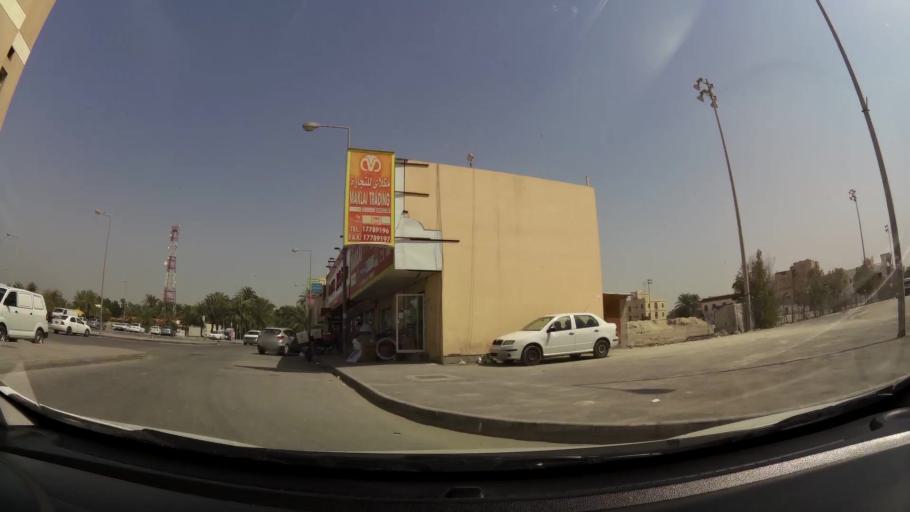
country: BH
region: Manama
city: Jidd Hafs
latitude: 26.2117
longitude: 50.4504
